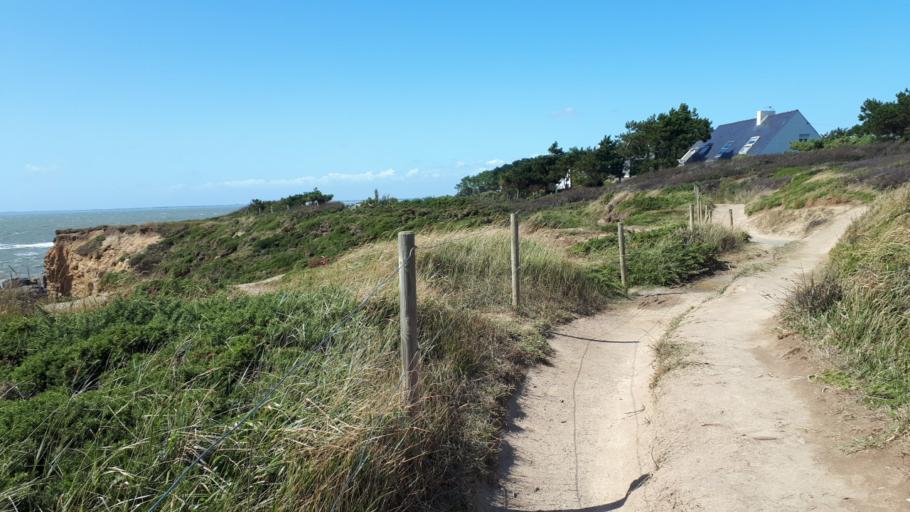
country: FR
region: Brittany
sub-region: Departement du Morbihan
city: Penestin
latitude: 47.4472
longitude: -2.4911
